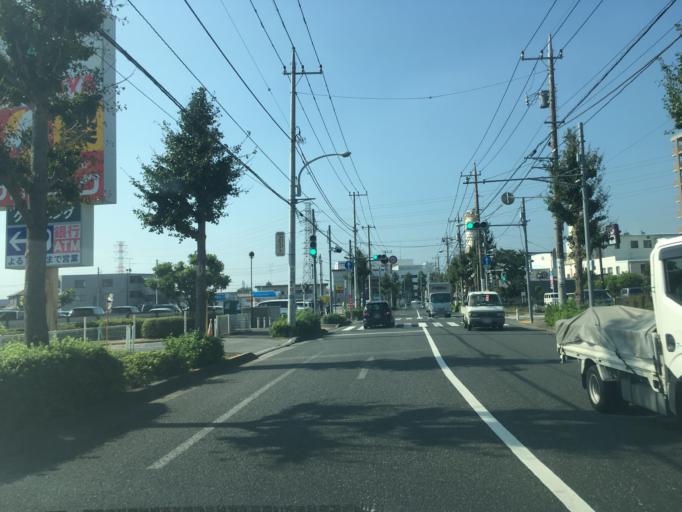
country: JP
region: Tokyo
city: Hino
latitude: 35.7200
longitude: 139.3833
